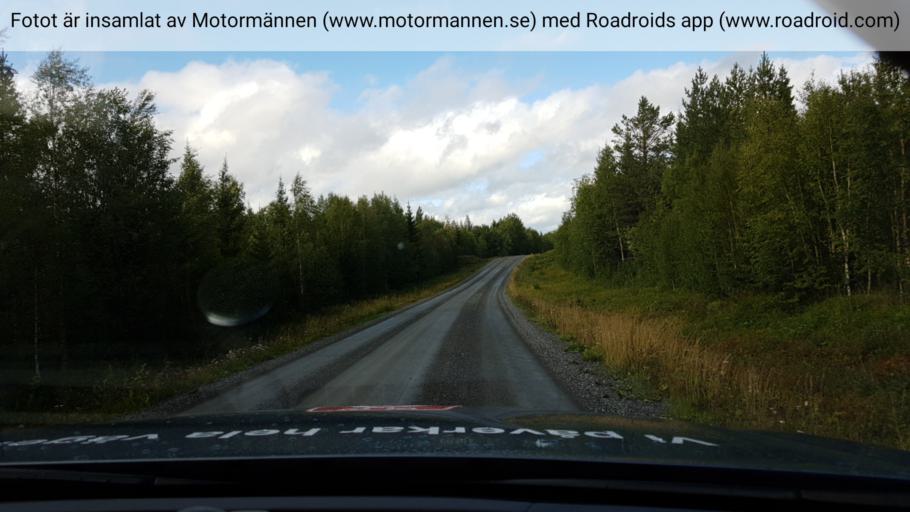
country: SE
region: Jaemtland
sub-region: Krokoms Kommun
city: Krokom
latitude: 63.7165
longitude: 14.5175
